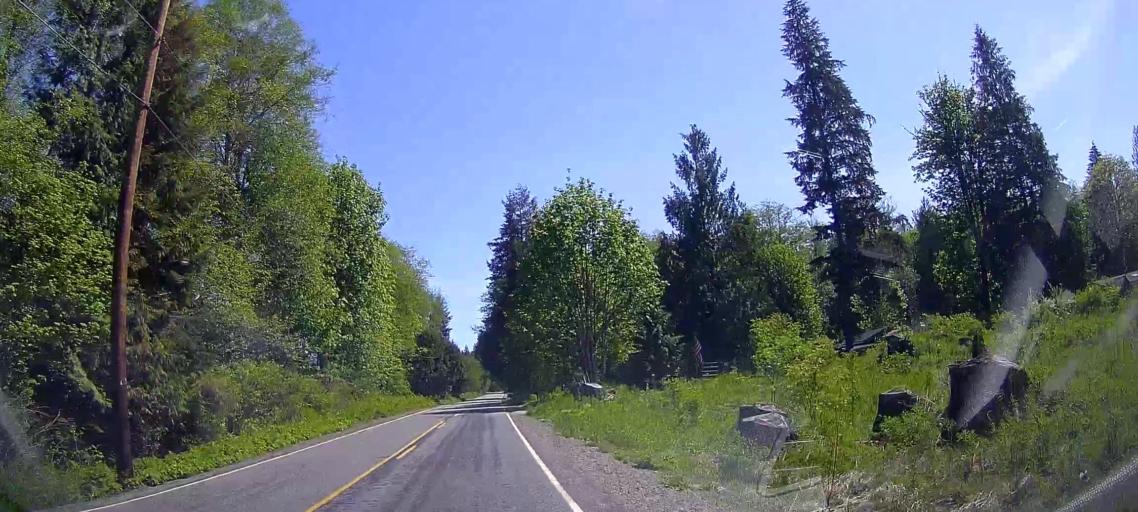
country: US
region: Washington
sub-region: Snohomish County
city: Darrington
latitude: 48.4728
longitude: -121.6378
